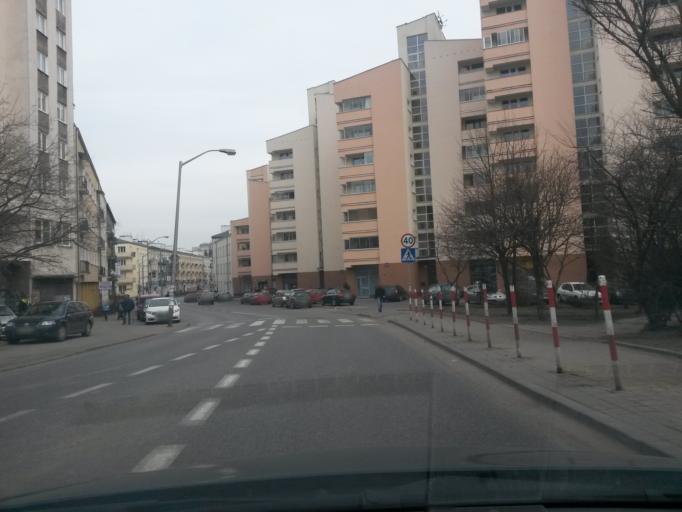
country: PL
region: Masovian Voivodeship
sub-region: Warszawa
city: Mokotow
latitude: 52.1999
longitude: 21.0279
